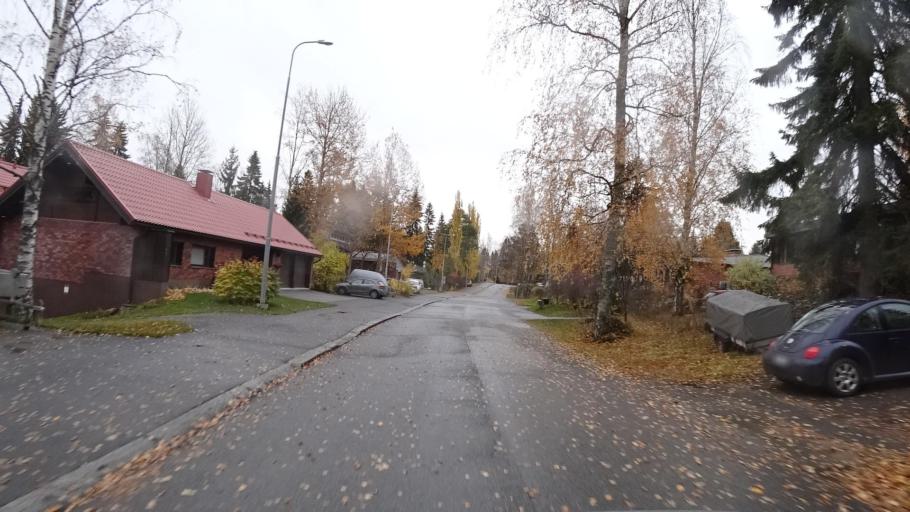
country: FI
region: Northern Savo
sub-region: Kuopio
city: Kuopio
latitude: 62.9288
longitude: 27.6934
